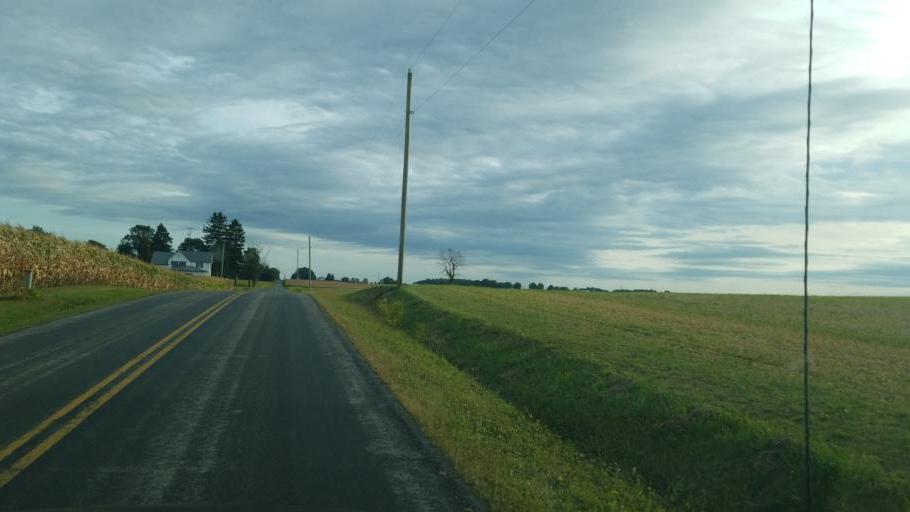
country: US
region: Ohio
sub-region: Crawford County
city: Bucyrus
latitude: 40.8690
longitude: -82.9018
